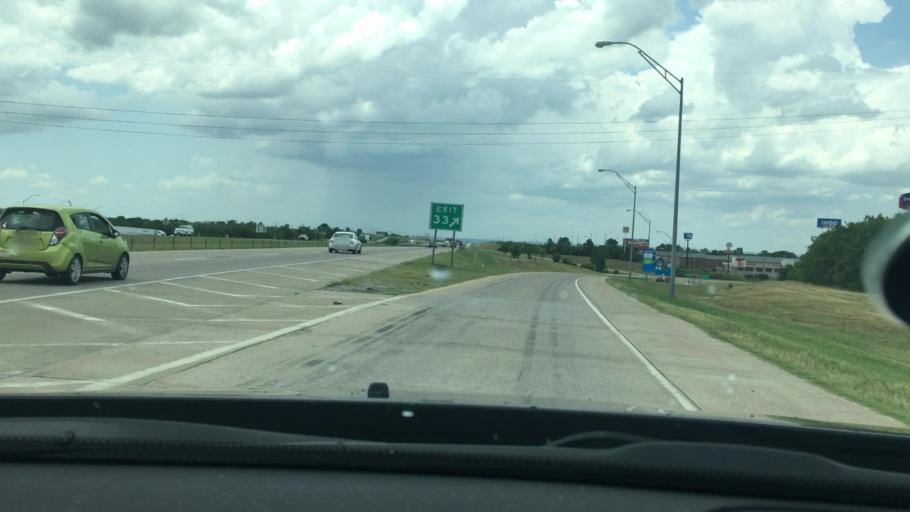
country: US
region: Oklahoma
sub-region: Carter County
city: Ardmore
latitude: 34.1986
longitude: -97.1637
